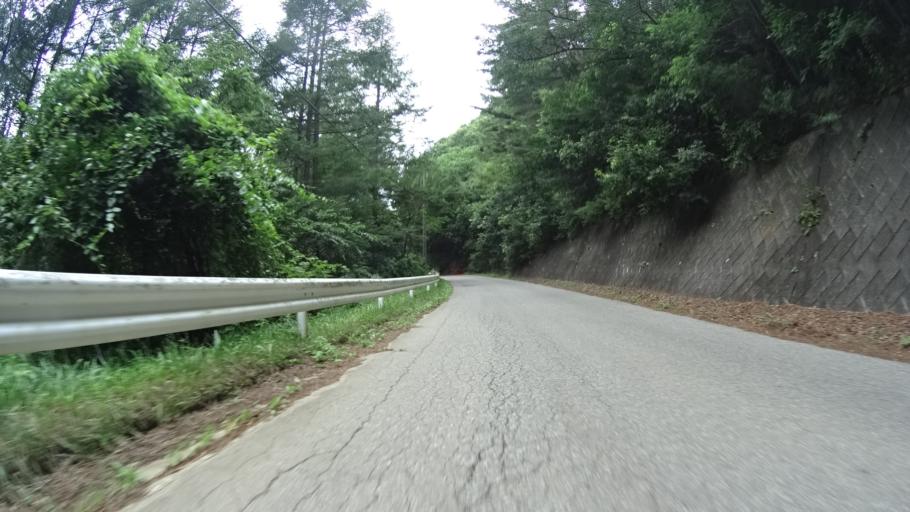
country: JP
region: Nagano
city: Saku
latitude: 36.0704
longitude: 138.6203
